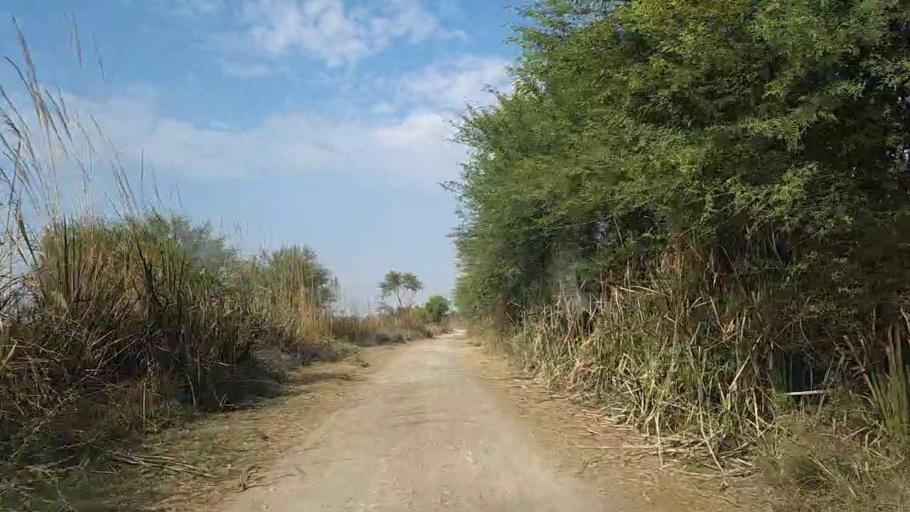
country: PK
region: Sindh
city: Sanghar
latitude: 26.2554
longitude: 69.0097
